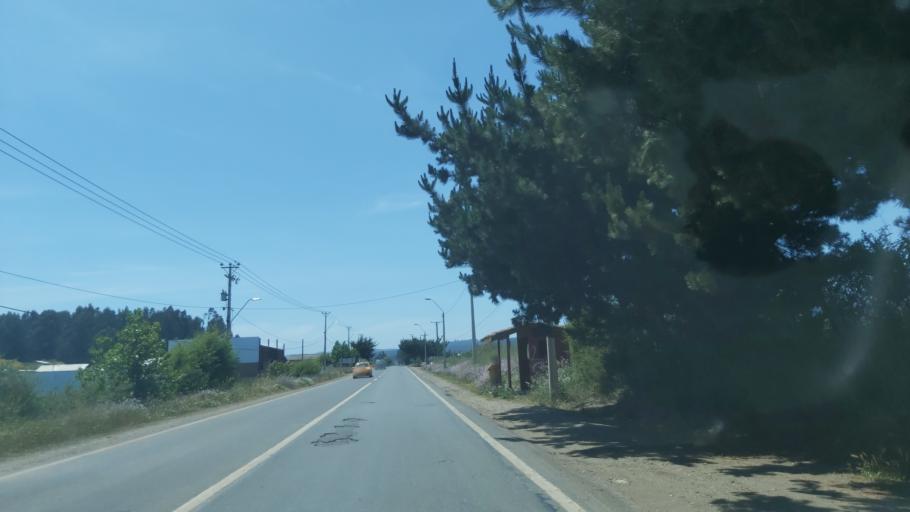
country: CL
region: Maule
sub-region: Provincia de Cauquenes
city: Cauquenes
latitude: -35.7990
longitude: -72.5622
